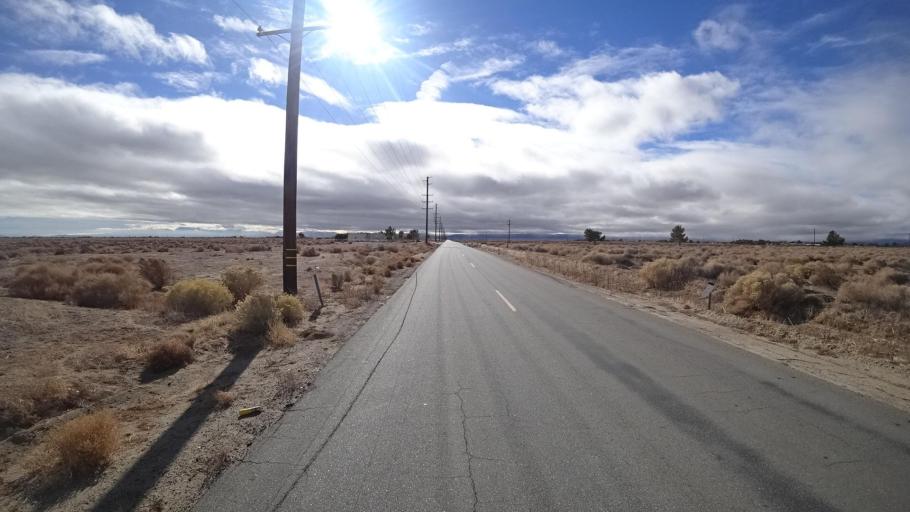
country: US
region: California
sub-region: Kern County
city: Rosamond
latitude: 34.8414
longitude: -118.2378
